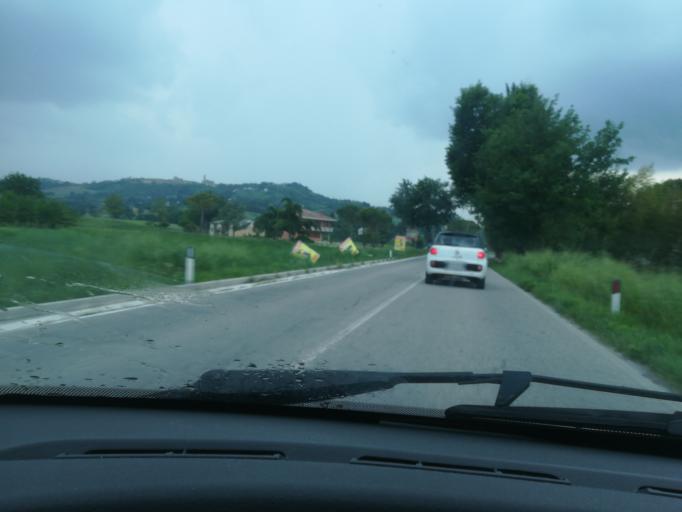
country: IT
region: The Marches
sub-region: Provincia di Macerata
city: Pollenza
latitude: 43.2876
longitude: 13.3562
